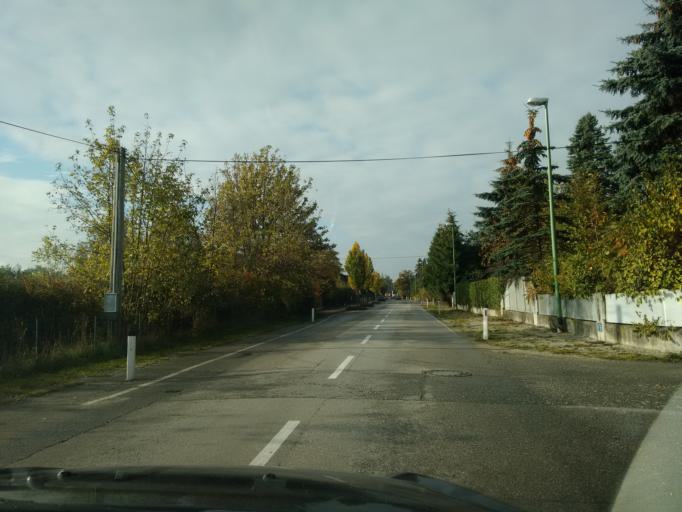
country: AT
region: Upper Austria
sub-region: Wels Stadt
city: Wels
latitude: 48.1668
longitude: 13.9892
